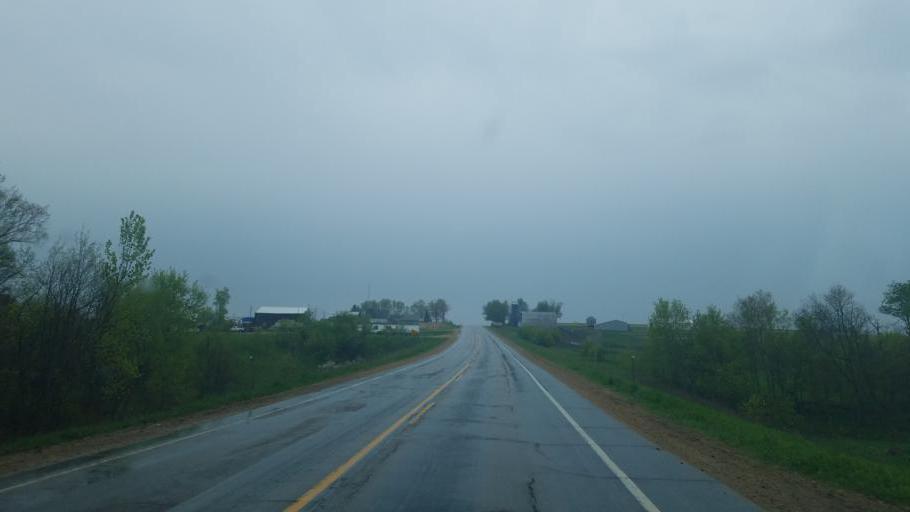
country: US
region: Wisconsin
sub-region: Vernon County
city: Hillsboro
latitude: 43.5918
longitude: -90.3522
